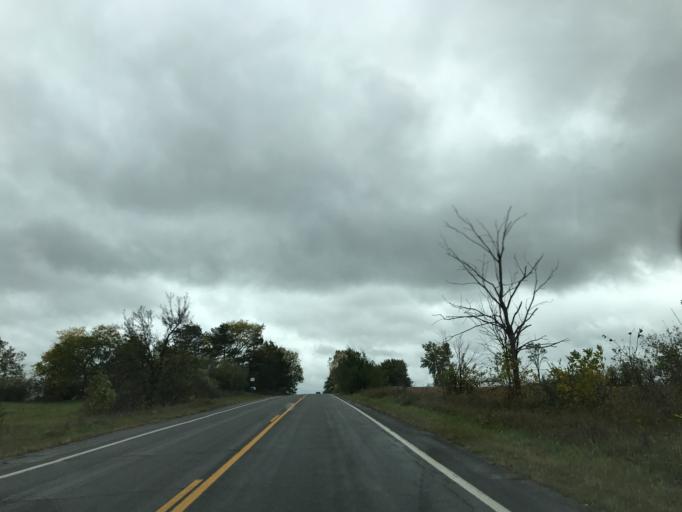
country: US
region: Michigan
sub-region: Oakland County
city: South Lyon
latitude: 42.3601
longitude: -83.6626
